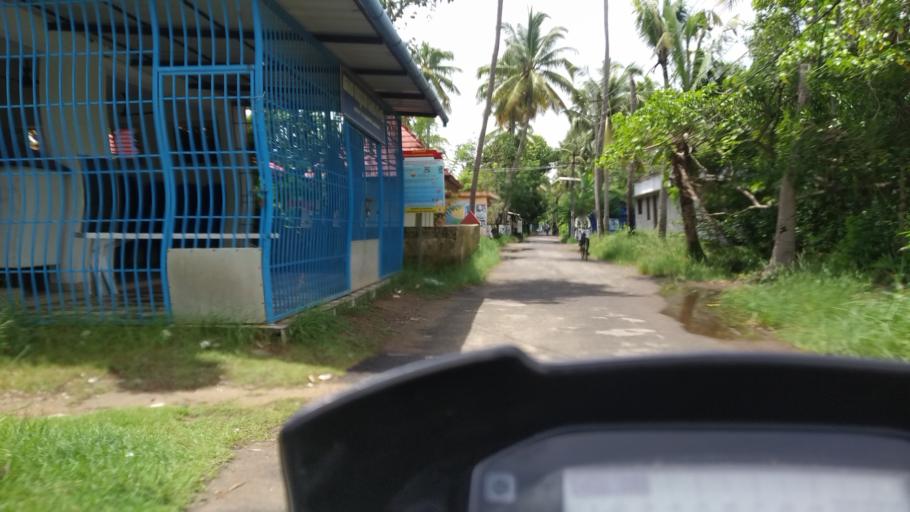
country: IN
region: Kerala
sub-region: Ernakulam
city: Elur
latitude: 10.0848
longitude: 76.2029
